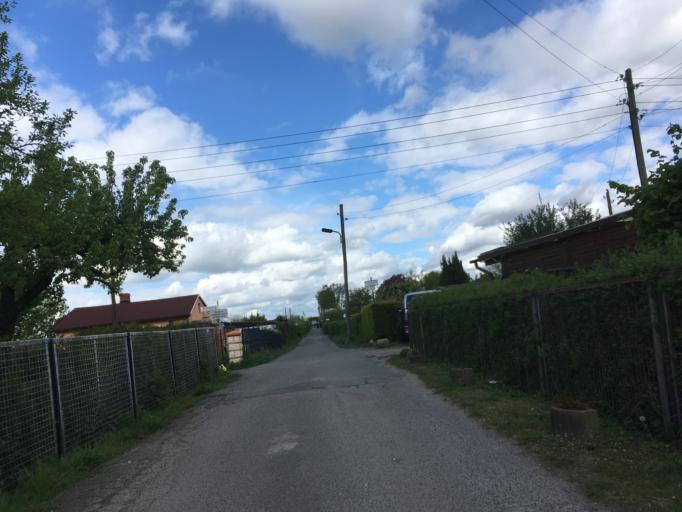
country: DE
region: Berlin
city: Buchholz
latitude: 52.6156
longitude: 13.4220
